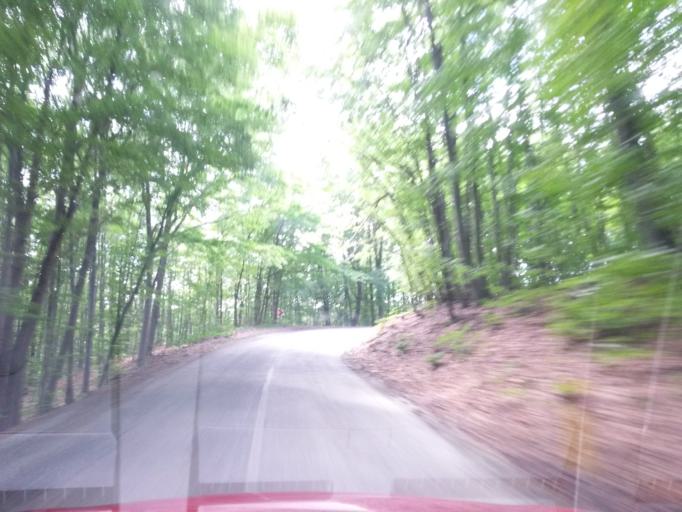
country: SK
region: Presovsky
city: Sabinov
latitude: 48.9511
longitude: 21.0662
